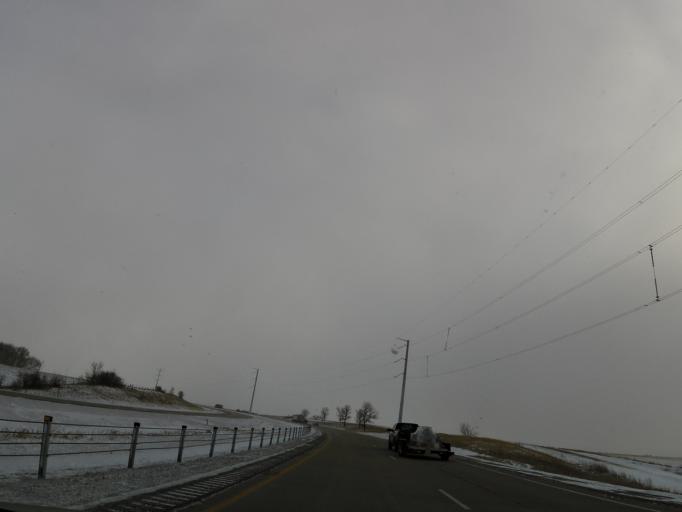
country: US
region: Minnesota
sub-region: Grant County
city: Elbow Lake
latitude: 46.0931
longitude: -95.8947
